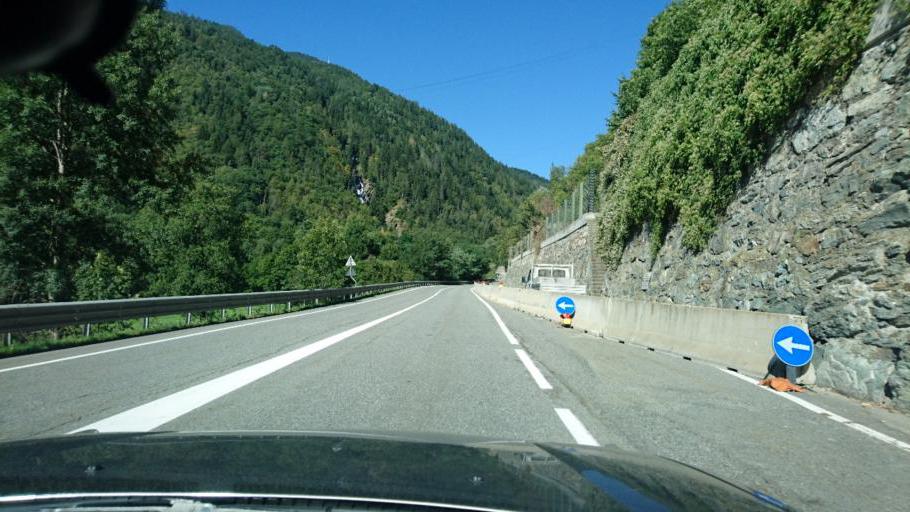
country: IT
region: Aosta Valley
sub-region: Valle d'Aosta
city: La Salle
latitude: 45.7308
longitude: 7.0828
